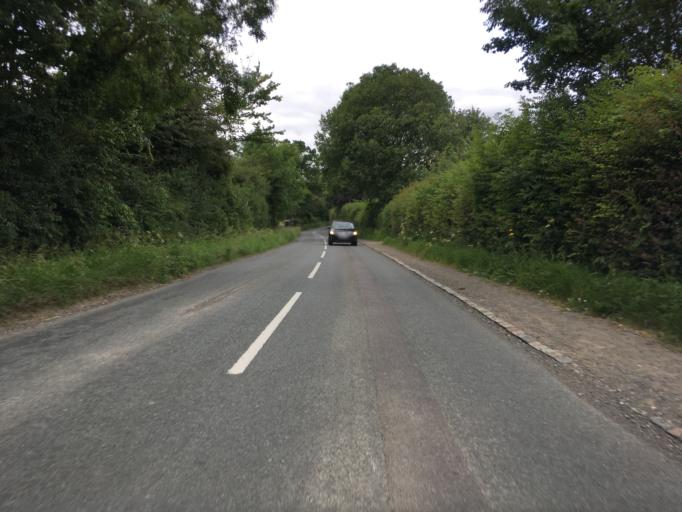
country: GB
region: England
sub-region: Gloucestershire
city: Bourton on the Water
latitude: 51.8760
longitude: -1.7349
